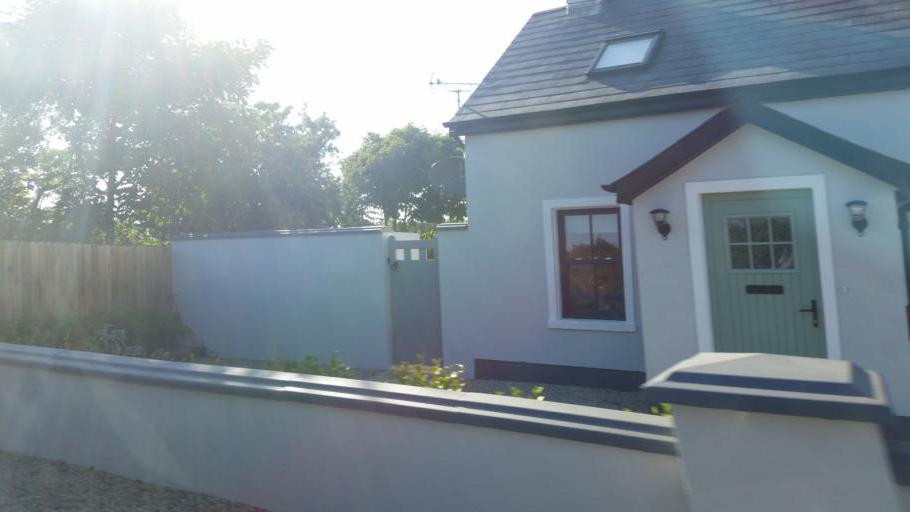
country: IE
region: Munster
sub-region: Waterford
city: Dunmore East
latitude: 52.2382
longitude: -6.8582
